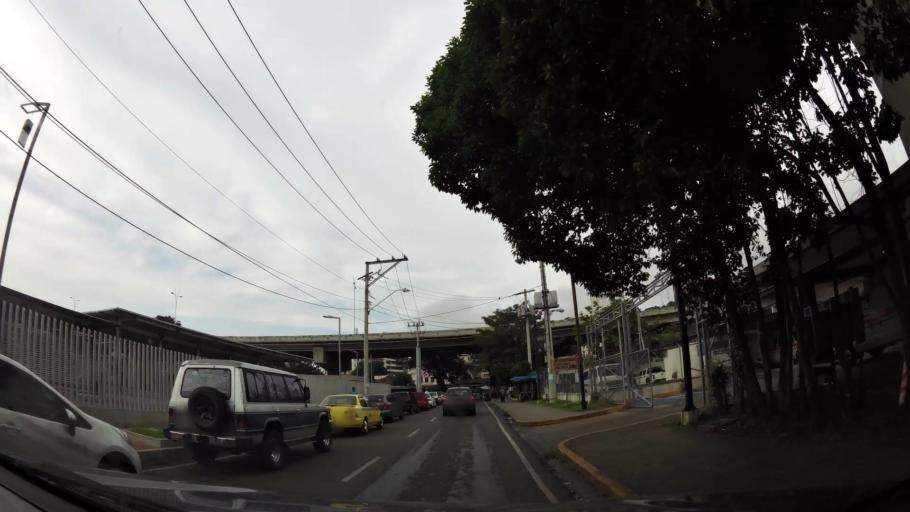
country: PA
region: Panama
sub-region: Distrito de Panama
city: Ancon
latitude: 8.9621
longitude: -79.5393
